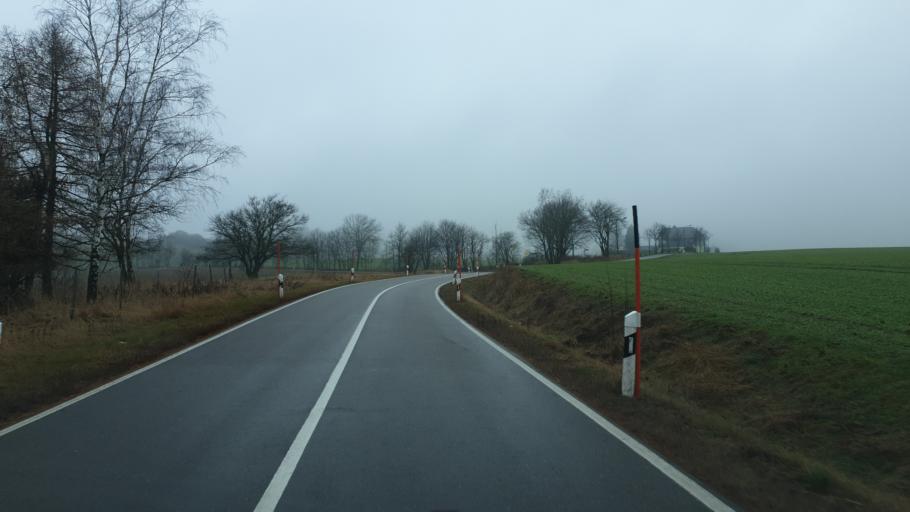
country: DE
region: Saxony
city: Neuhausen
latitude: 50.6656
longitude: 13.4735
